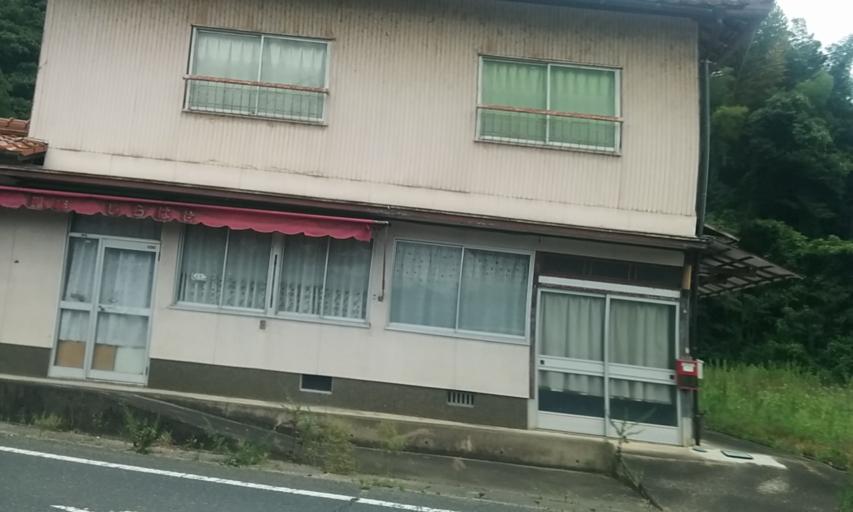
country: JP
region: Kyoto
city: Ayabe
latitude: 35.3425
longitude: 135.2166
